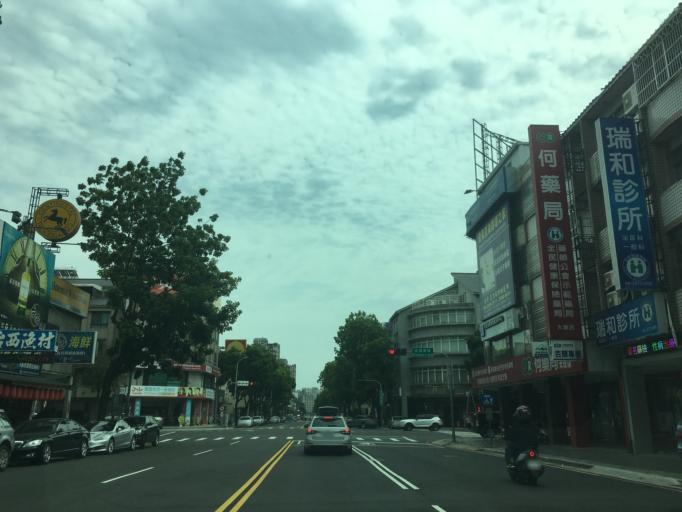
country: TW
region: Taiwan
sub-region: Taichung City
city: Taichung
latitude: 24.1355
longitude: 120.6499
